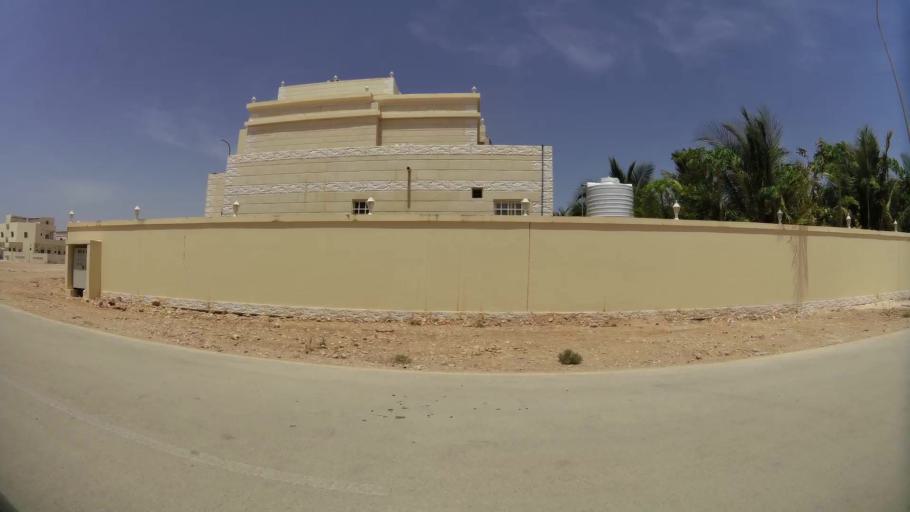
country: OM
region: Zufar
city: Salalah
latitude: 17.0662
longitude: 54.1483
